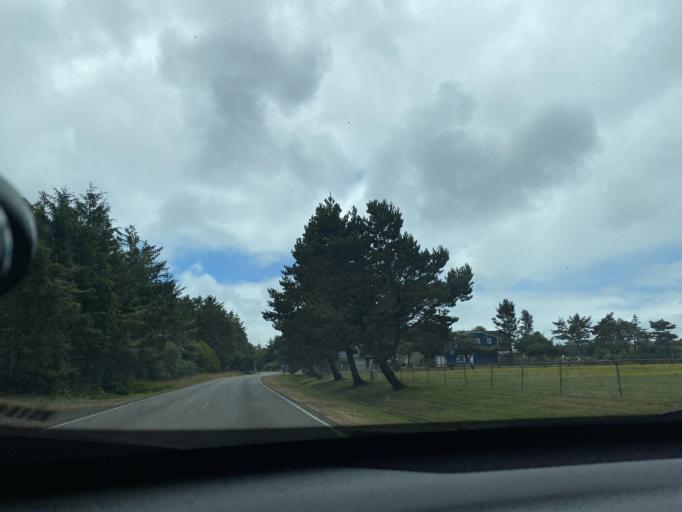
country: US
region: Washington
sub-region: Grays Harbor County
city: Ocean Shores
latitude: 46.9714
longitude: -124.1402
